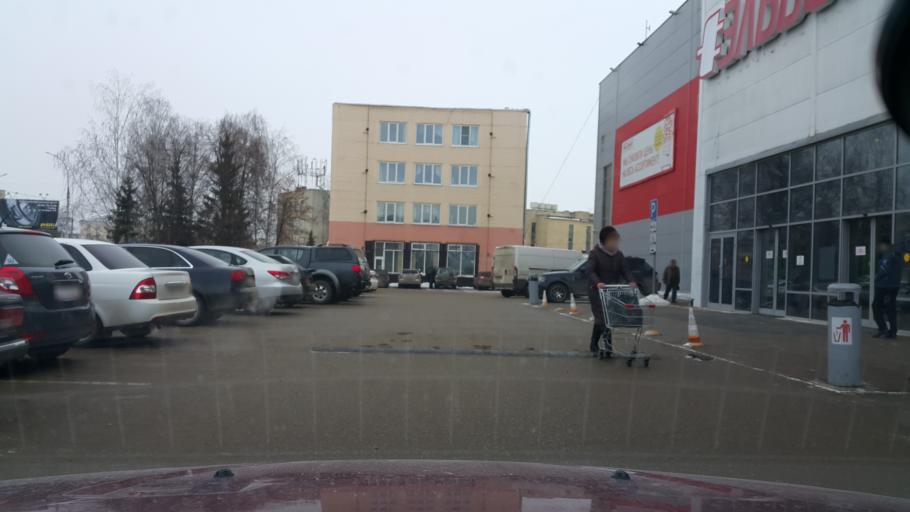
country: RU
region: Tambov
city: Tambov
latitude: 52.7454
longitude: 41.4491
